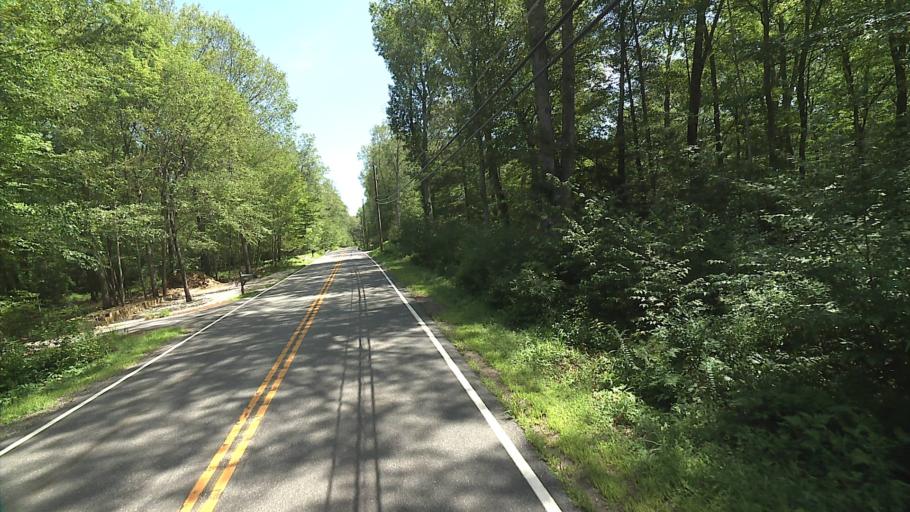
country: US
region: Connecticut
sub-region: Windham County
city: South Woodstock
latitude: 41.8958
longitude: -72.0522
